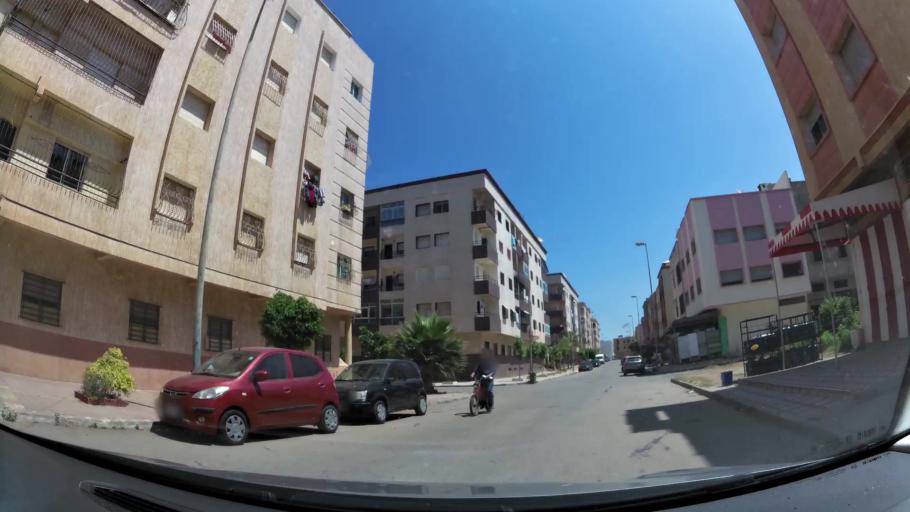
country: MA
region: Rabat-Sale-Zemmour-Zaer
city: Sale
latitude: 34.0776
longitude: -6.7895
